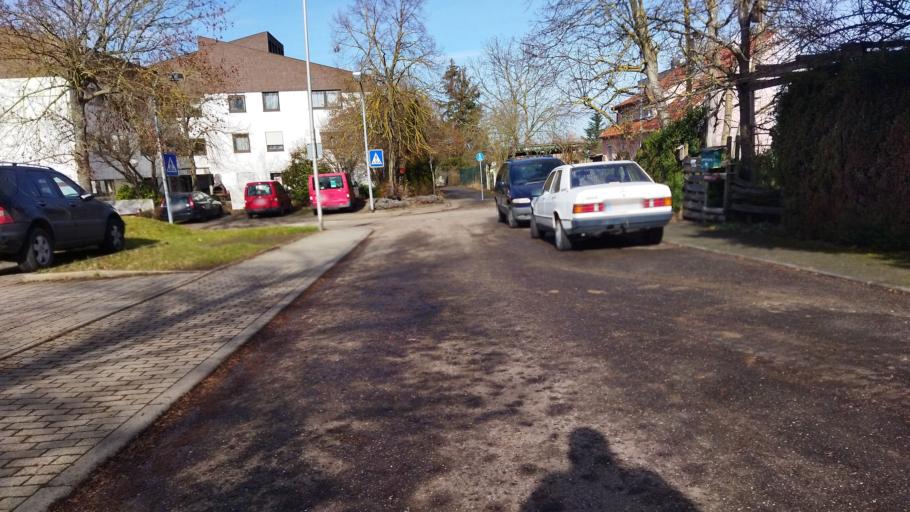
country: DE
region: Baden-Wuerttemberg
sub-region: Regierungsbezirk Stuttgart
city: Heilbronn
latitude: 49.1371
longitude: 9.1724
